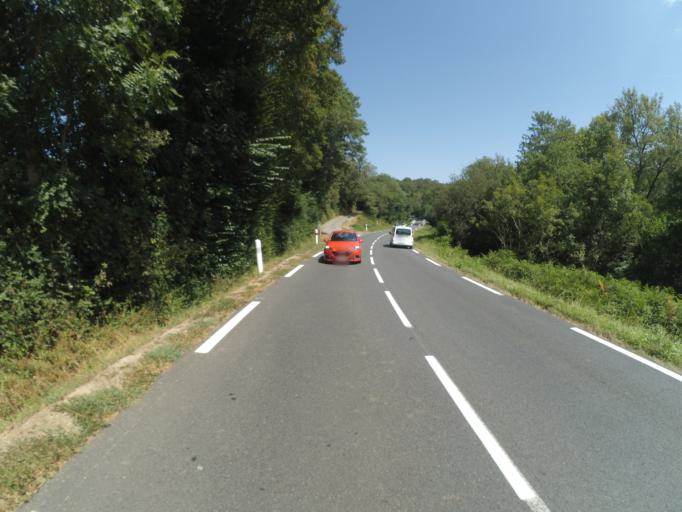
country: FR
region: Limousin
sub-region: Departement de la Haute-Vienne
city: Bussiere-Poitevine
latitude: 46.2330
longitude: 0.9299
